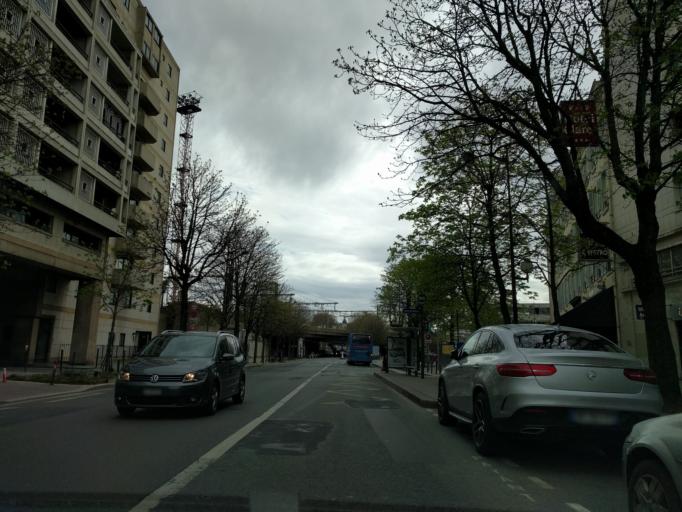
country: FR
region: Ile-de-France
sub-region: Departement du Val-de-Marne
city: Ivry-sur-Seine
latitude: 48.8401
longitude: 2.3811
